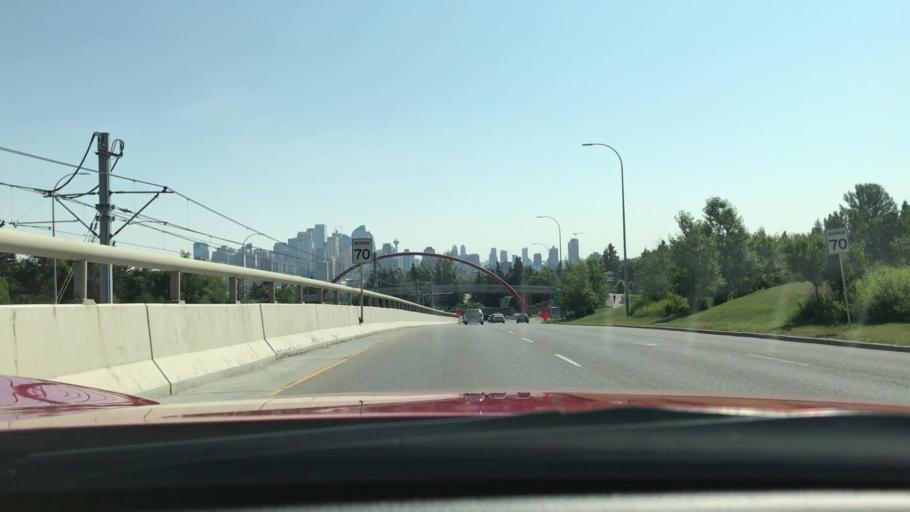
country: CA
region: Alberta
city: Calgary
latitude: 51.0415
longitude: -114.1221
